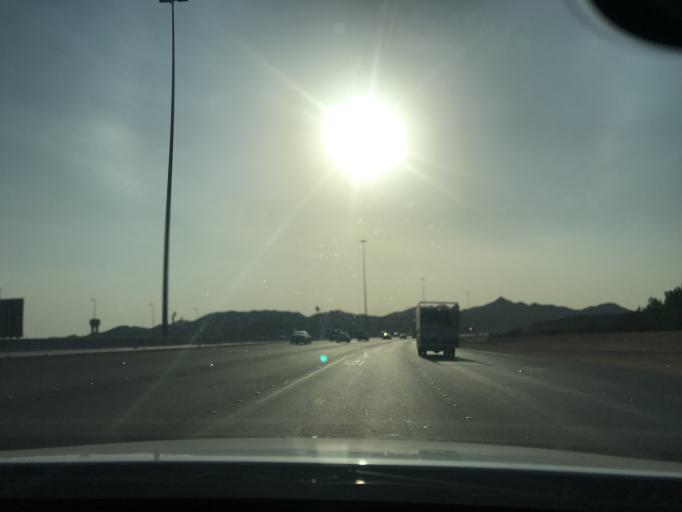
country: SA
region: Makkah
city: Jeddah
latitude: 21.3895
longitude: 39.4197
